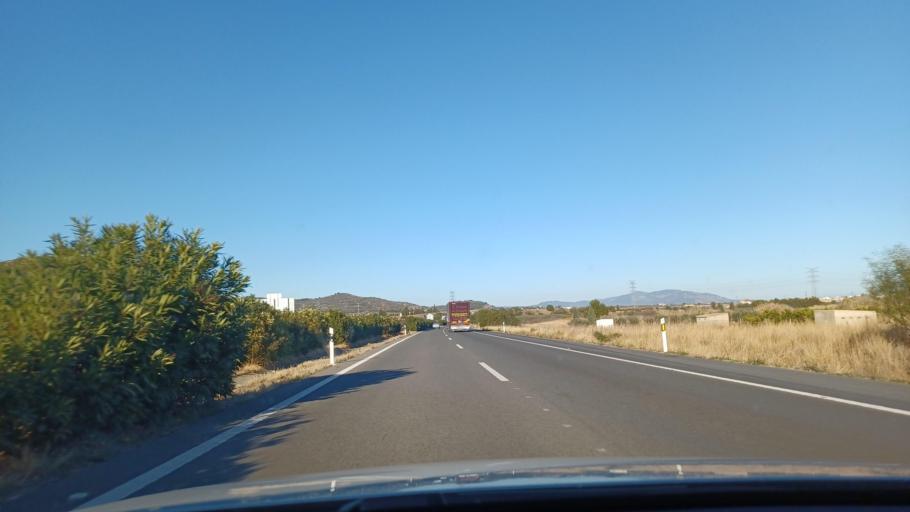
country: ES
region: Valencia
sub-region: Provincia de Castello
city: Orpesa/Oropesa del Mar
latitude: 40.1438
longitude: 0.1441
